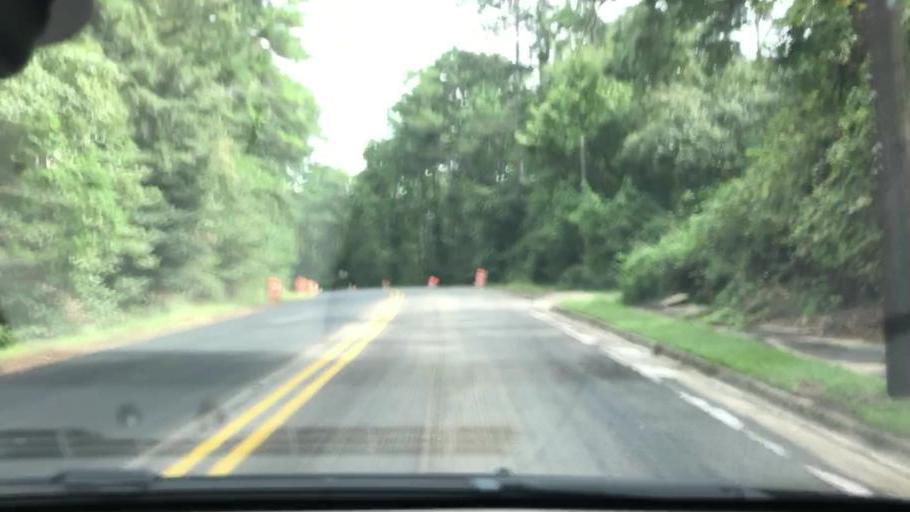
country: US
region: Georgia
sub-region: Clay County
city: Fort Gaines
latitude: 31.5972
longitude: -85.0458
